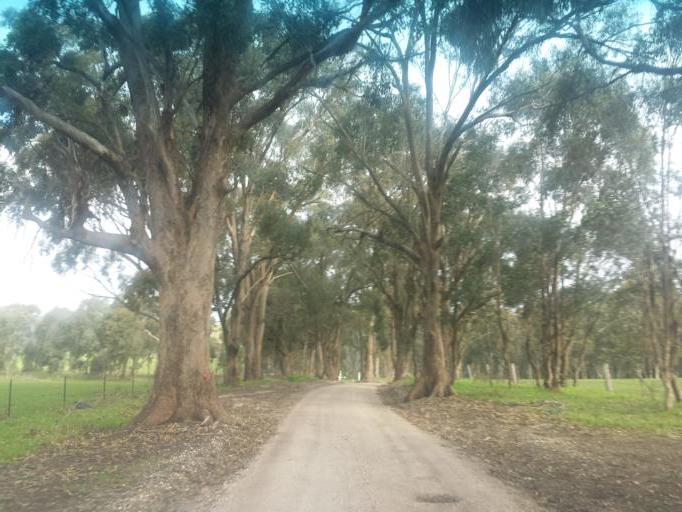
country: AU
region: Victoria
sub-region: Murrindindi
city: Kinglake West
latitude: -37.0454
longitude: 145.2319
